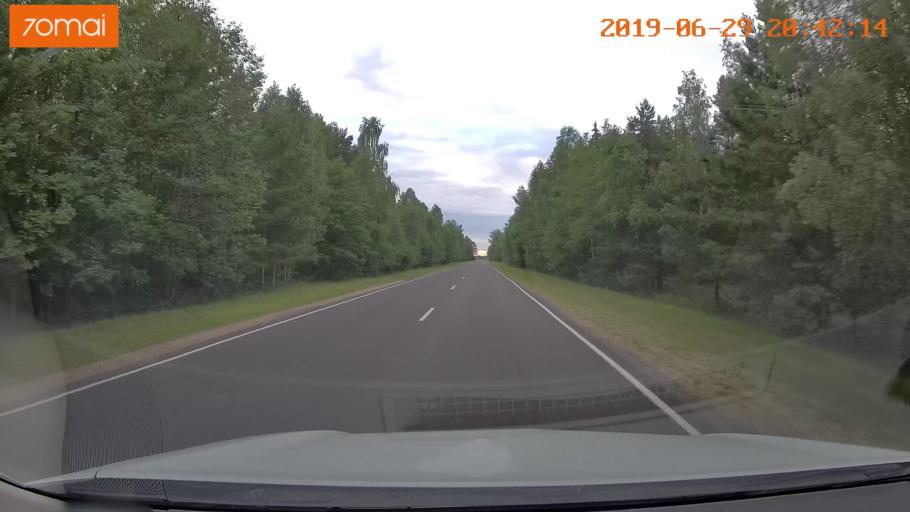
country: BY
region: Brest
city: Hantsavichy
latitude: 52.5953
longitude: 26.3289
